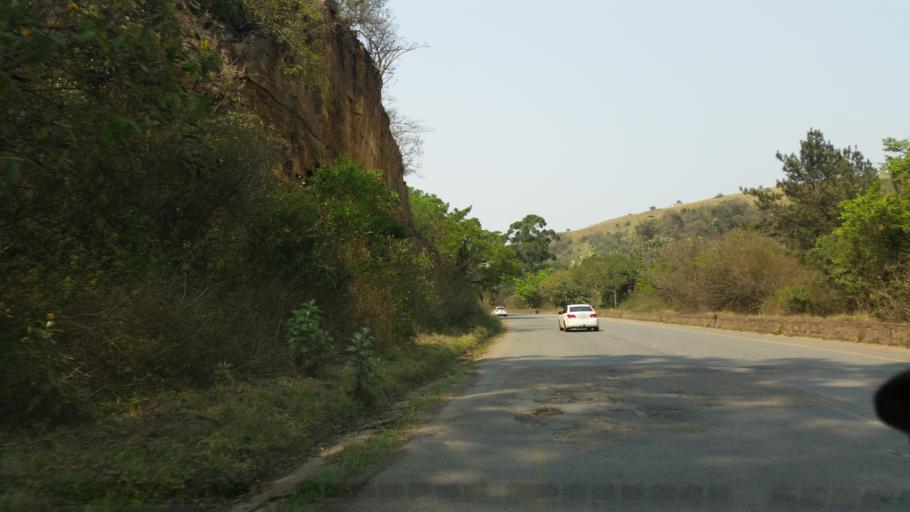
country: ZA
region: KwaZulu-Natal
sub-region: eThekwini Metropolitan Municipality
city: Mpumalanga
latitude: -29.7448
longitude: 30.6643
